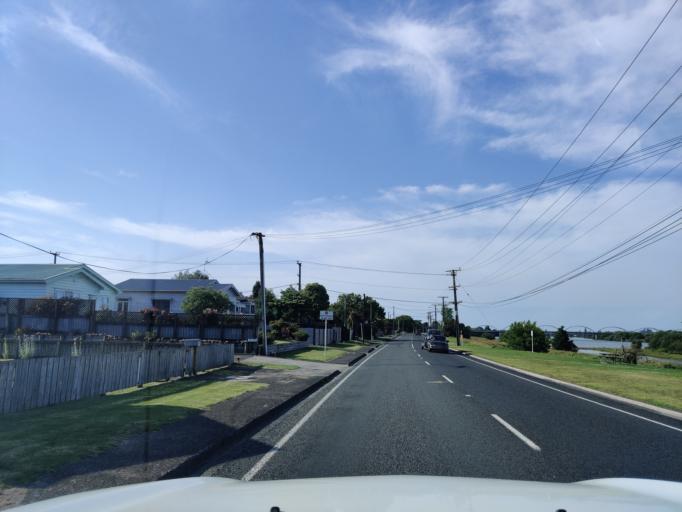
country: NZ
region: Waikato
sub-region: Waikato District
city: Ngaruawahia
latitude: -37.5735
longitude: 175.1526
